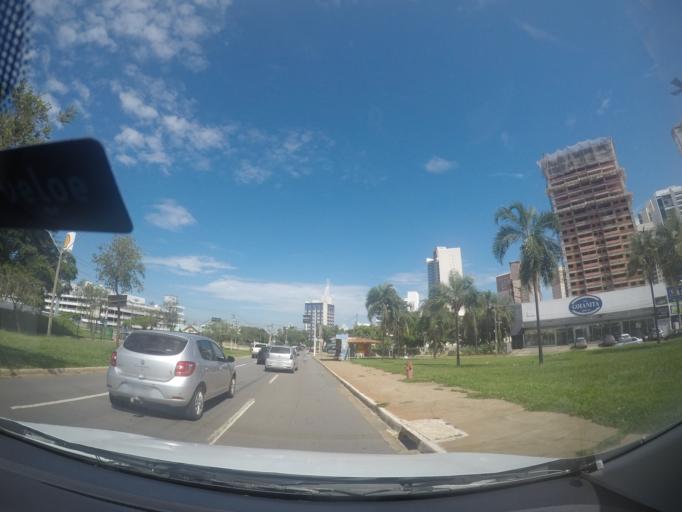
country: BR
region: Goias
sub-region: Goiania
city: Goiania
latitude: -16.7085
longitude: -49.2344
